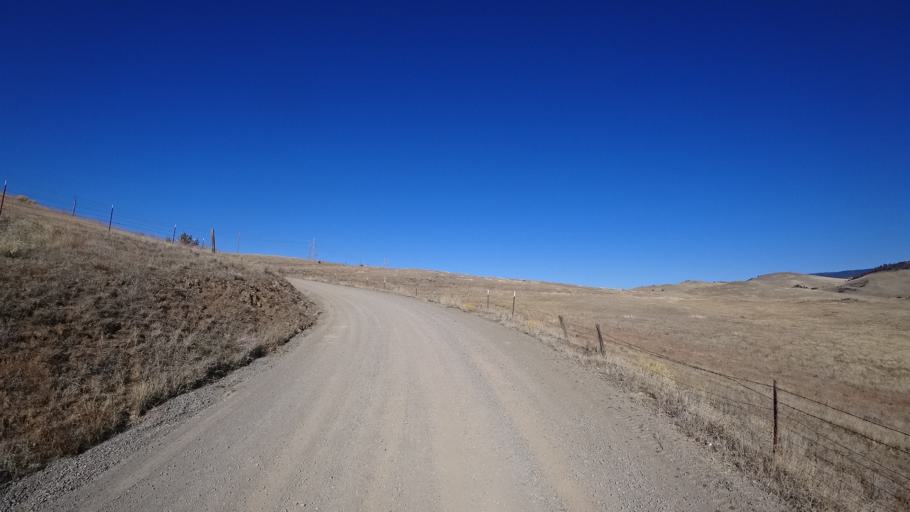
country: US
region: California
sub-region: Siskiyou County
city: Montague
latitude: 41.7670
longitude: -122.3572
